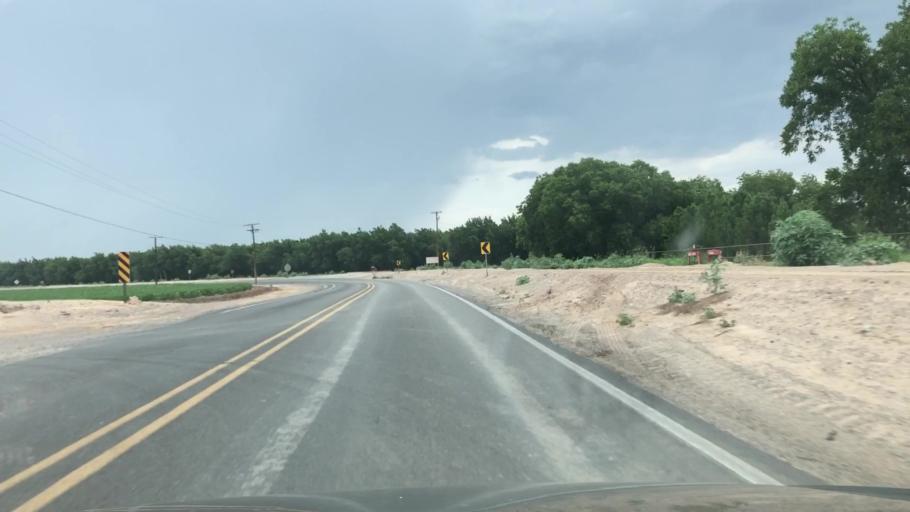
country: US
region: New Mexico
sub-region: Dona Ana County
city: La Union
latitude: 31.9849
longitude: -106.6501
